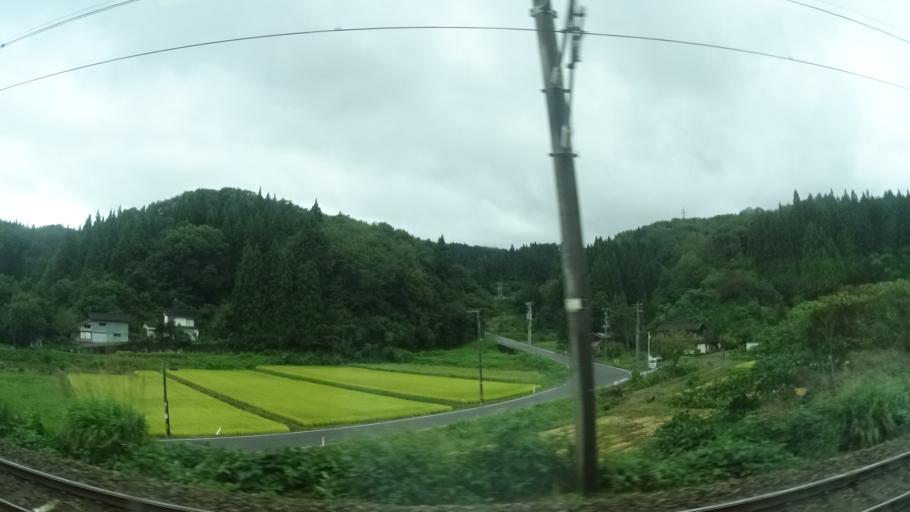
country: JP
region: Yamagata
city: Tsuruoka
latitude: 38.7017
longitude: 139.7092
